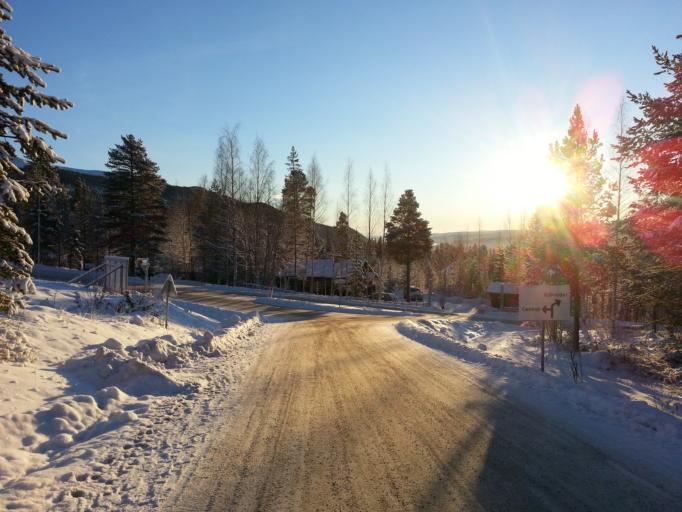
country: SE
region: Jaemtland
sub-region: Harjedalens Kommun
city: Sveg
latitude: 62.4237
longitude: 13.9485
